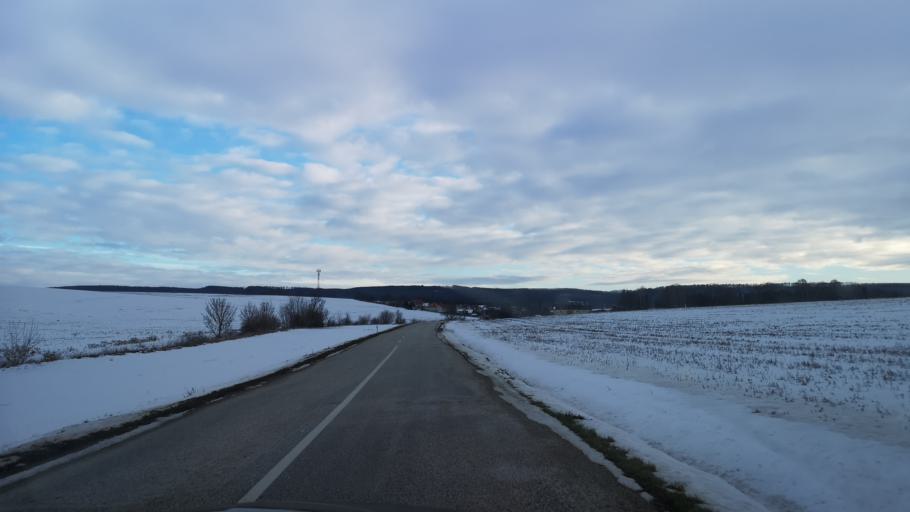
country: SK
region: Nitriansky
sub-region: Okres Nitra
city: Vrable
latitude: 48.1182
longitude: 18.3345
